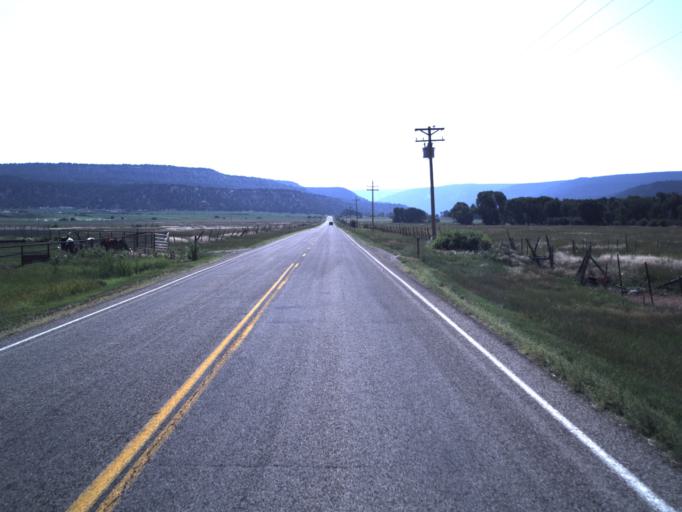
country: US
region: Utah
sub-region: Duchesne County
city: Duchesne
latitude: 40.3426
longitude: -110.6951
